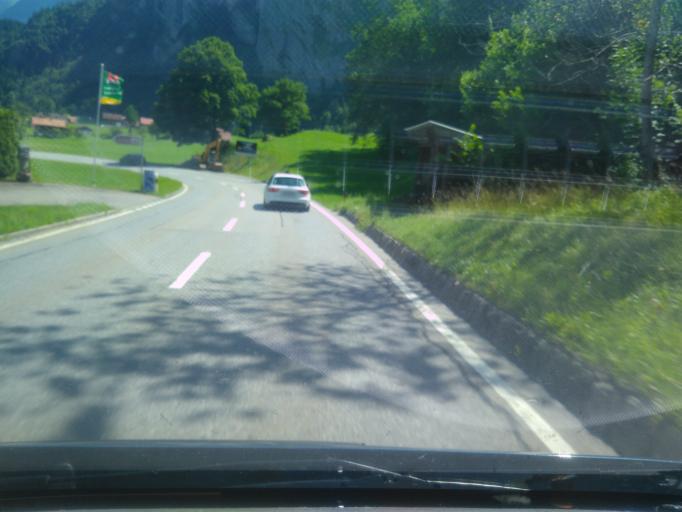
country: CH
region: Bern
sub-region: Interlaken-Oberhasli District
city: Meiringen
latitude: 46.7094
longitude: 8.2145
